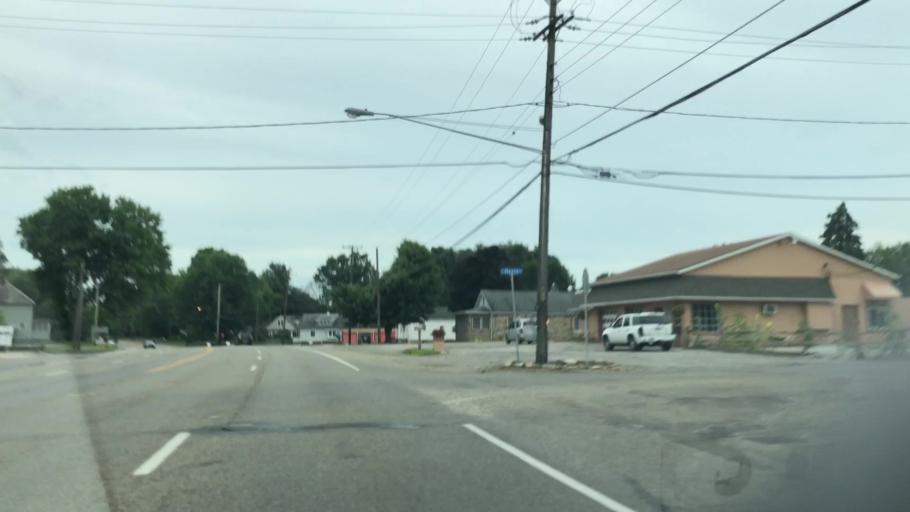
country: US
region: Ohio
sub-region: Stark County
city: Uniontown
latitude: 41.0030
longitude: -81.4091
